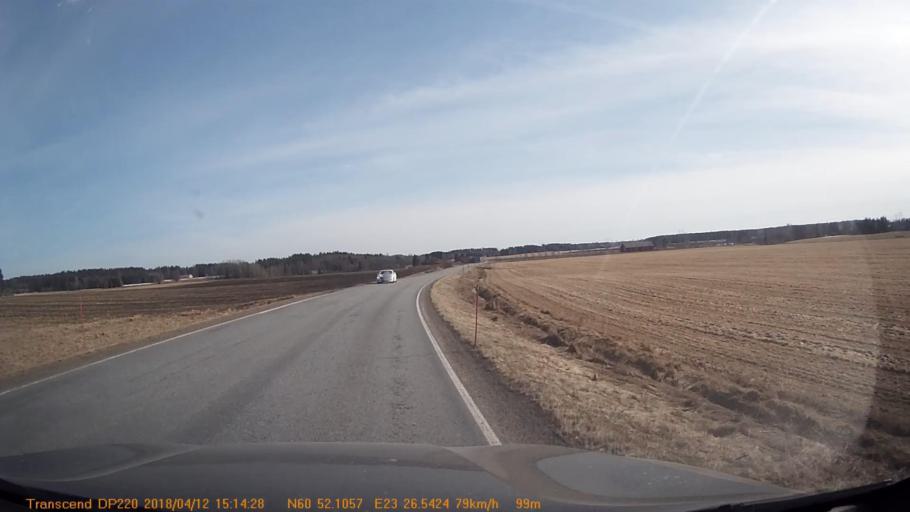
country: FI
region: Haeme
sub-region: Forssa
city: Jokioinen
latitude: 60.8683
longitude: 23.4426
